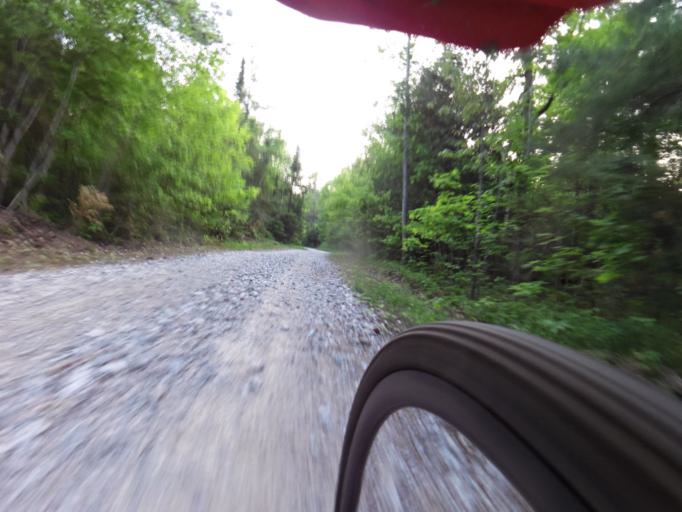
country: CA
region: Ontario
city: Arnprior
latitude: 45.1838
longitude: -76.5089
